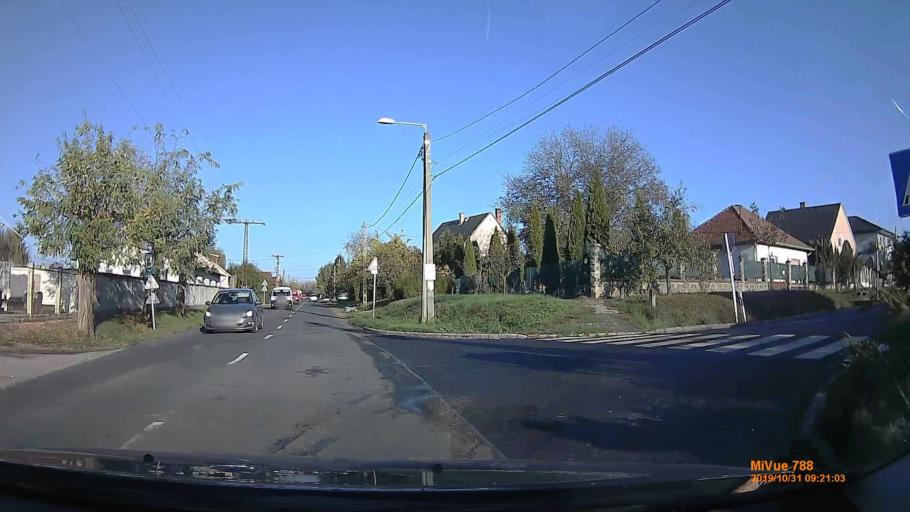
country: HU
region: Pest
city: Gyomro
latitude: 47.4282
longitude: 19.3828
